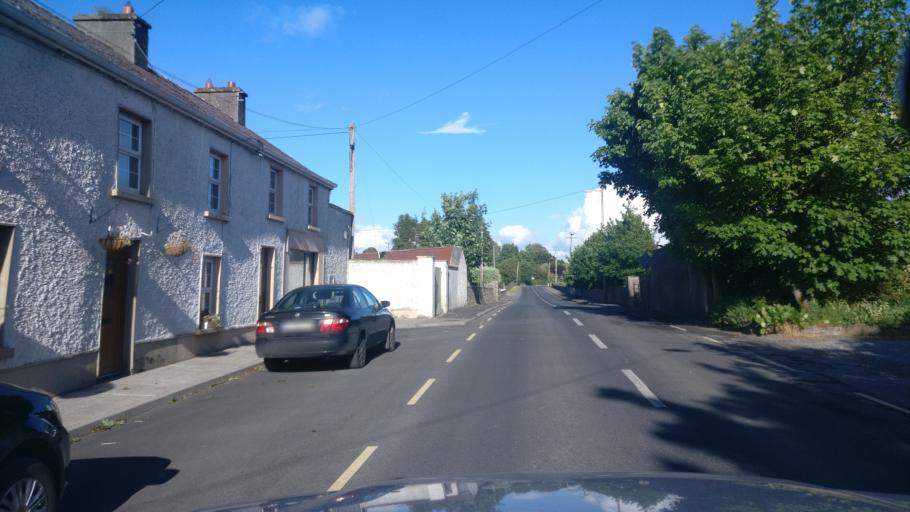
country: IE
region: Connaught
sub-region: County Galway
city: Ballinasloe
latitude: 53.2356
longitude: -8.2702
